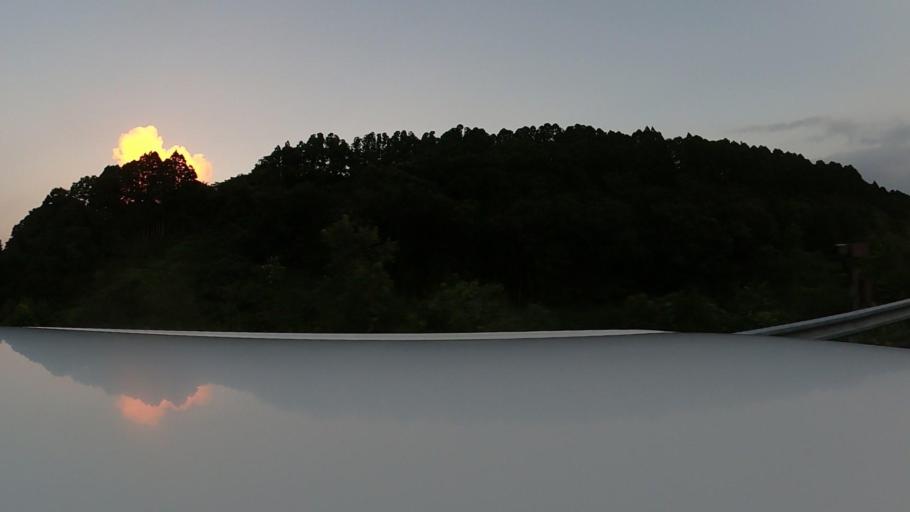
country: JP
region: Miyazaki
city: Takanabe
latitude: 32.3127
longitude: 131.5704
